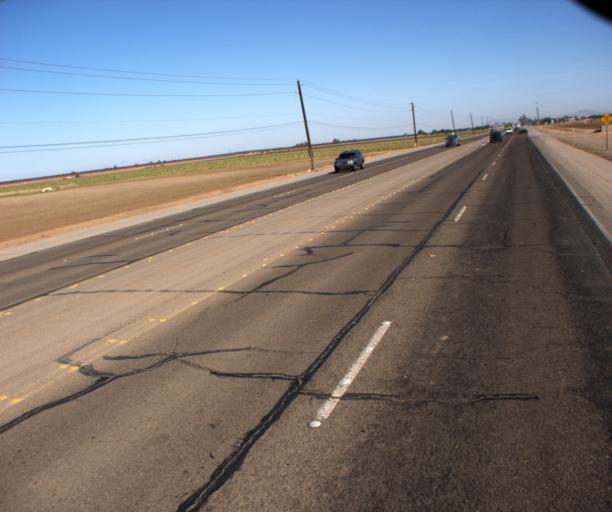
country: US
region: Arizona
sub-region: Yuma County
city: San Luis
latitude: 32.5367
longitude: -114.7868
